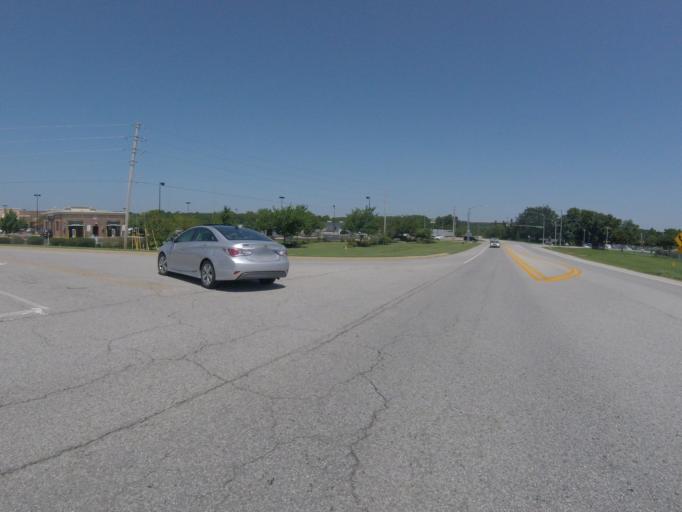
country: US
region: Arkansas
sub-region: Washington County
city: Johnson
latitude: 36.1078
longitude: -94.1802
